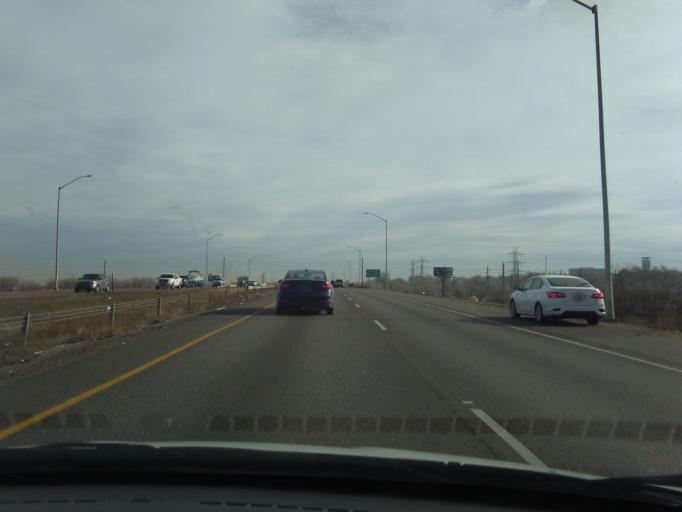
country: US
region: Colorado
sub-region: Adams County
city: Berkley
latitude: 39.7992
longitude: -105.0374
